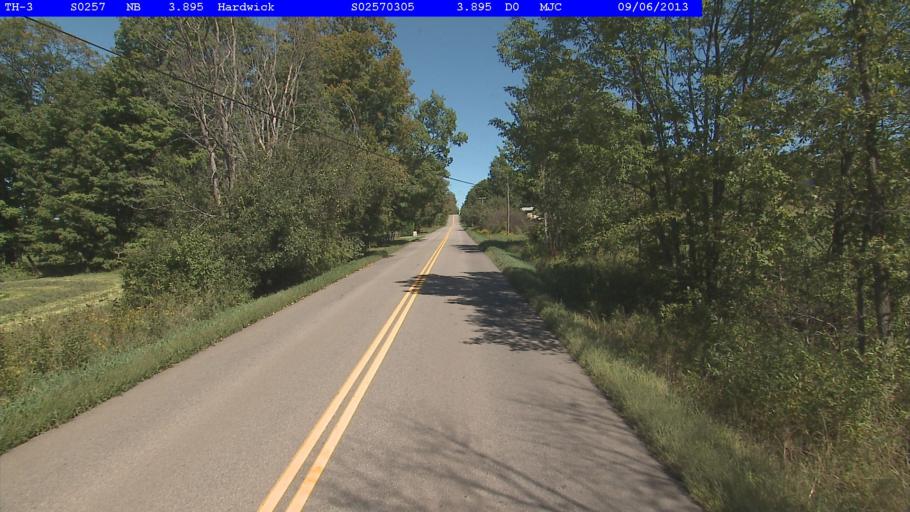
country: US
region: Vermont
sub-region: Caledonia County
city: Hardwick
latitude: 44.5444
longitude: -72.3248
